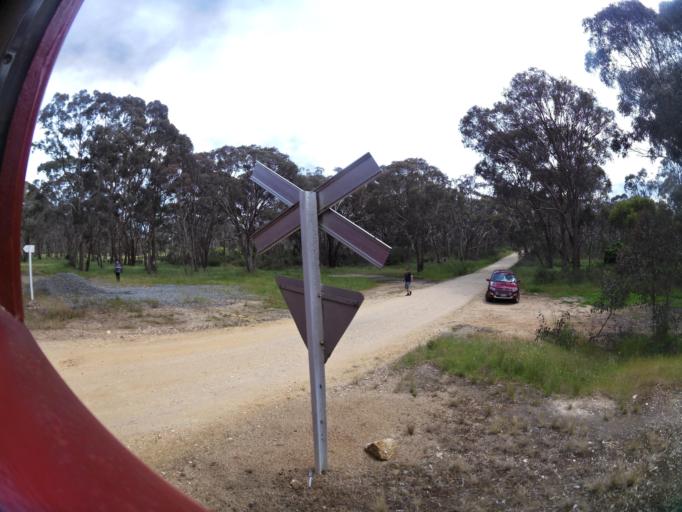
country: AU
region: Victoria
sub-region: Mount Alexander
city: Castlemaine
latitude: -36.9908
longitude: 144.0828
